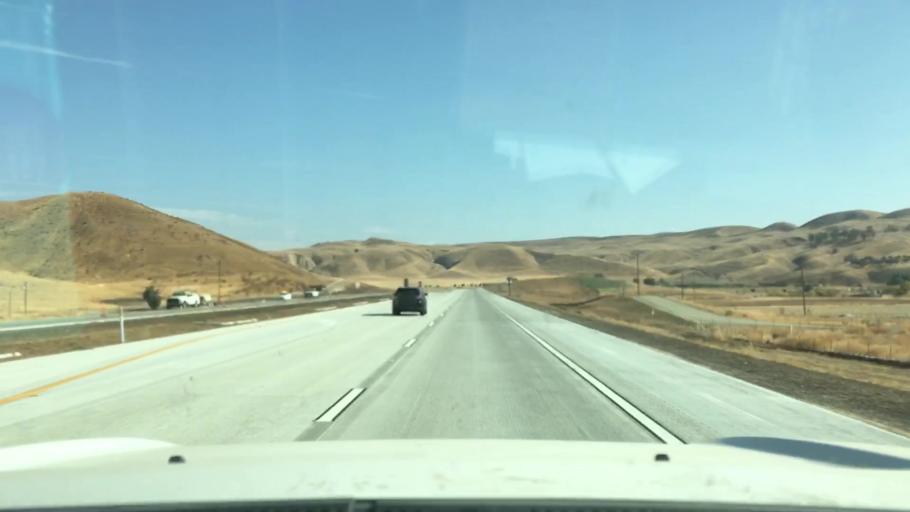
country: US
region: California
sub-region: San Luis Obispo County
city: Shandon
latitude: 35.6626
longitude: -120.3718
